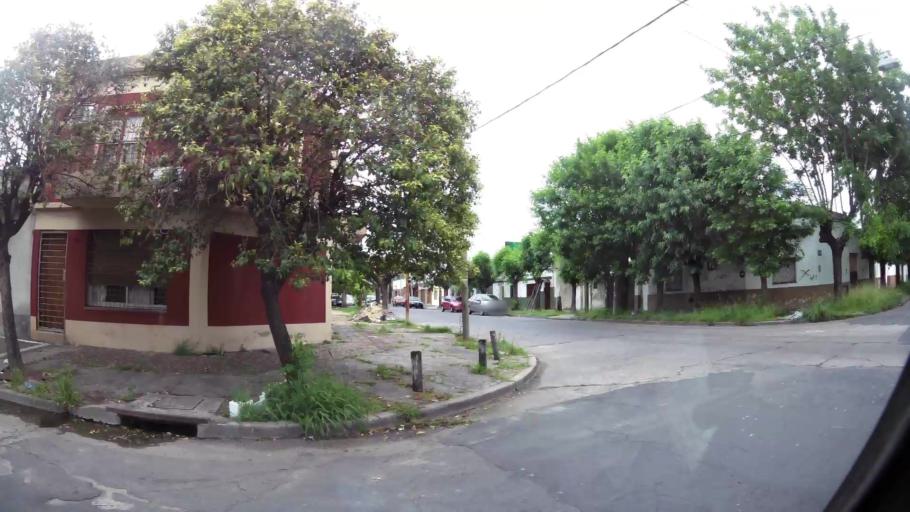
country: AR
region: Buenos Aires
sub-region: Partido de Lanus
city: Lanus
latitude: -34.6881
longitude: -58.3930
